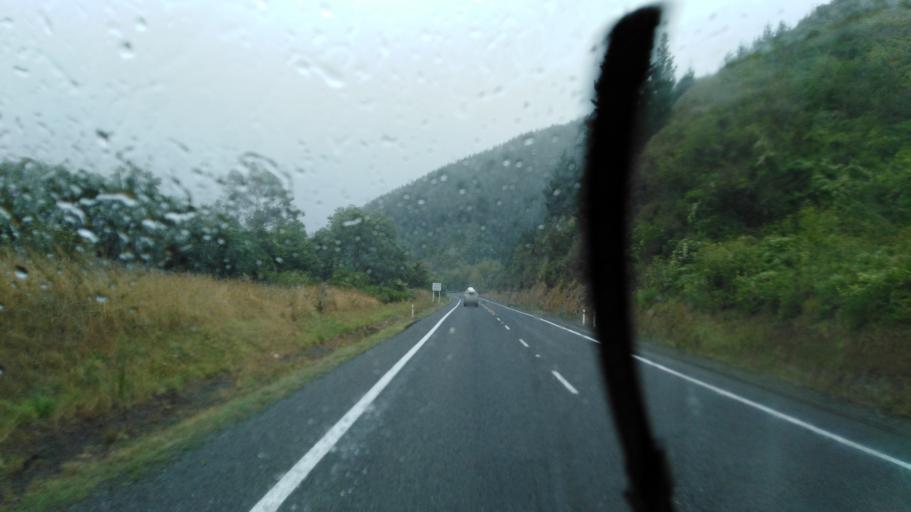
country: NZ
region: Marlborough
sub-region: Marlborough District
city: Picton
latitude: -41.3890
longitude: 173.9518
